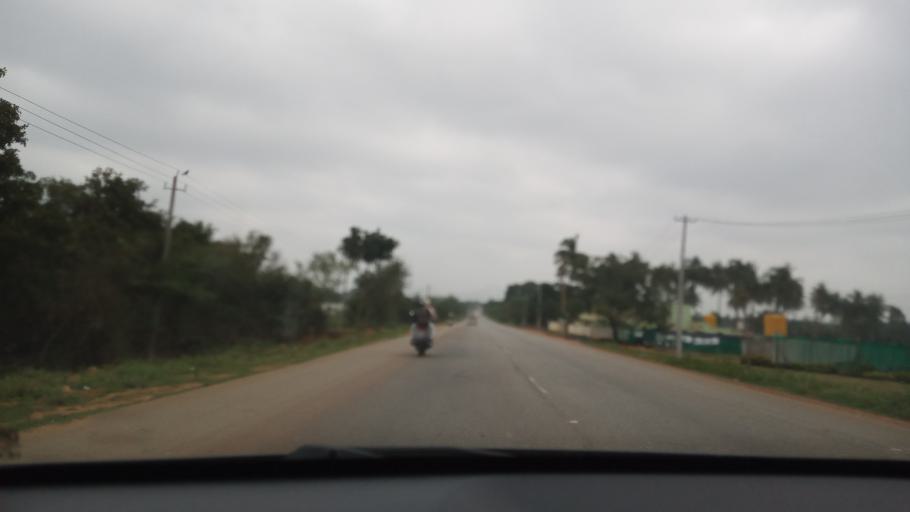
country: IN
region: Karnataka
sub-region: Chikkaballapur
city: Sidlaghatta
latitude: 13.2751
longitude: 77.9527
